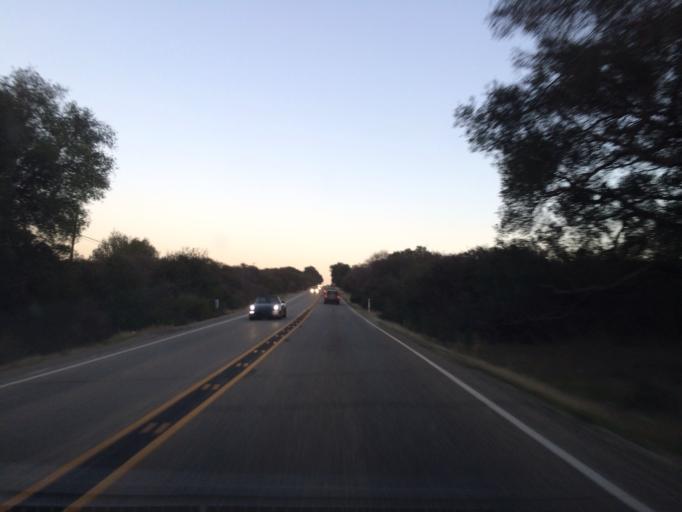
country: US
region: California
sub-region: Santa Barbara County
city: Santa Ynez
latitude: 34.5795
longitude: -119.9869
